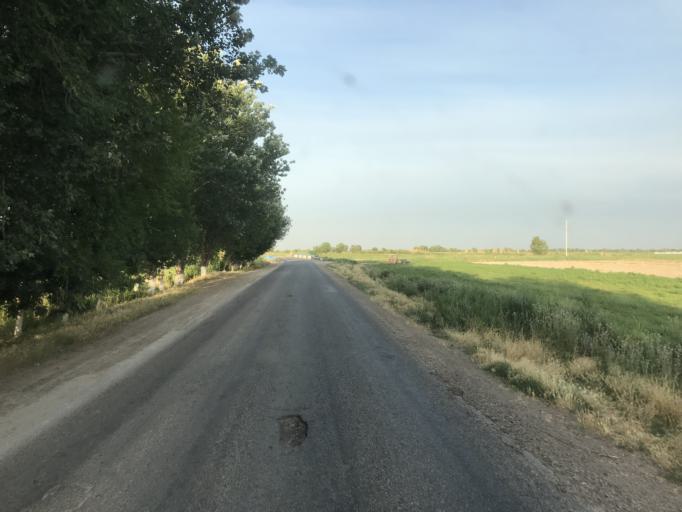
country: KZ
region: Ongtustik Qazaqstan
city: Asykata
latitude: 40.9511
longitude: 68.4517
